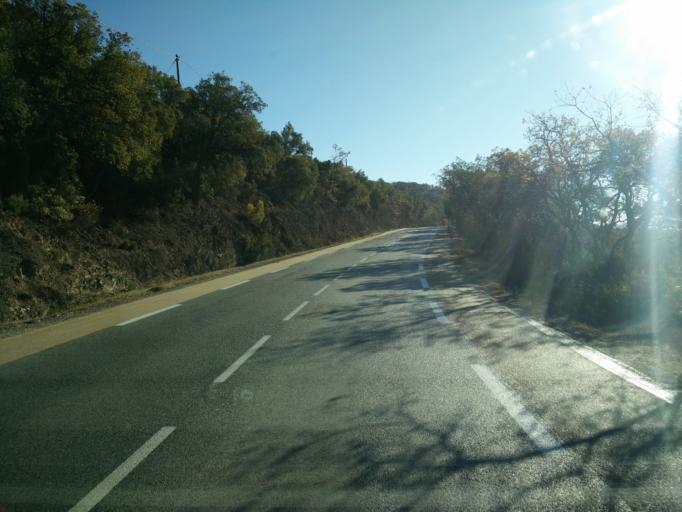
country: FR
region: Provence-Alpes-Cote d'Azur
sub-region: Departement du Var
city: Grimaud
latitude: 43.2846
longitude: 6.5039
